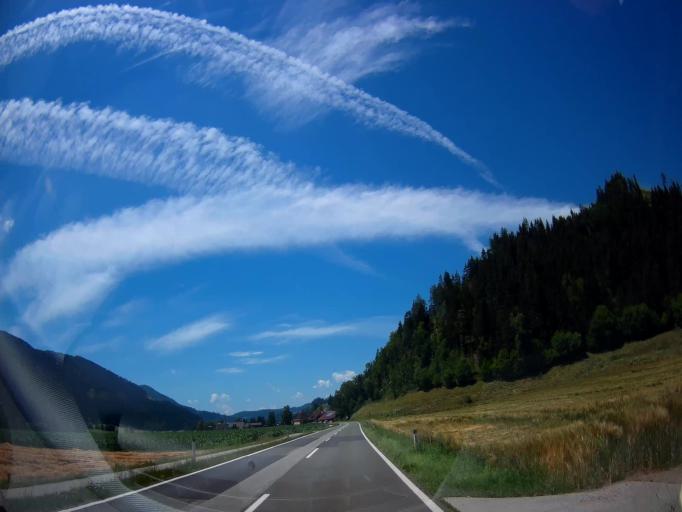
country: AT
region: Carinthia
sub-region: Politischer Bezirk Sankt Veit an der Glan
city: Micheldorf
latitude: 46.9029
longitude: 14.3926
